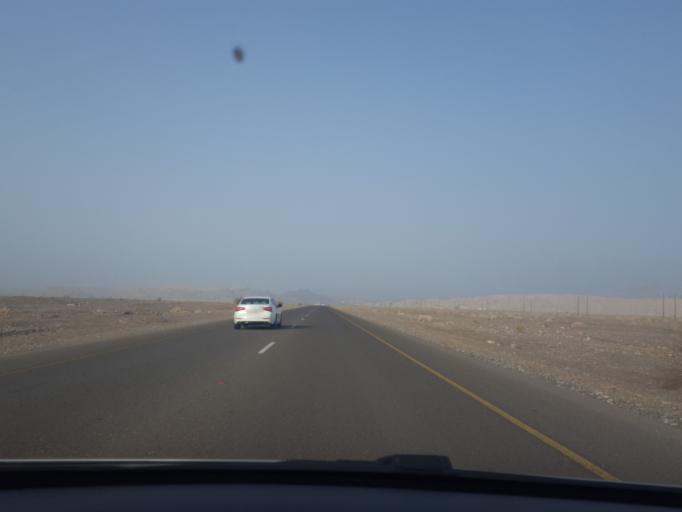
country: AE
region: Abu Dhabi
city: Al Ain
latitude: 24.0246
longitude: 55.9776
